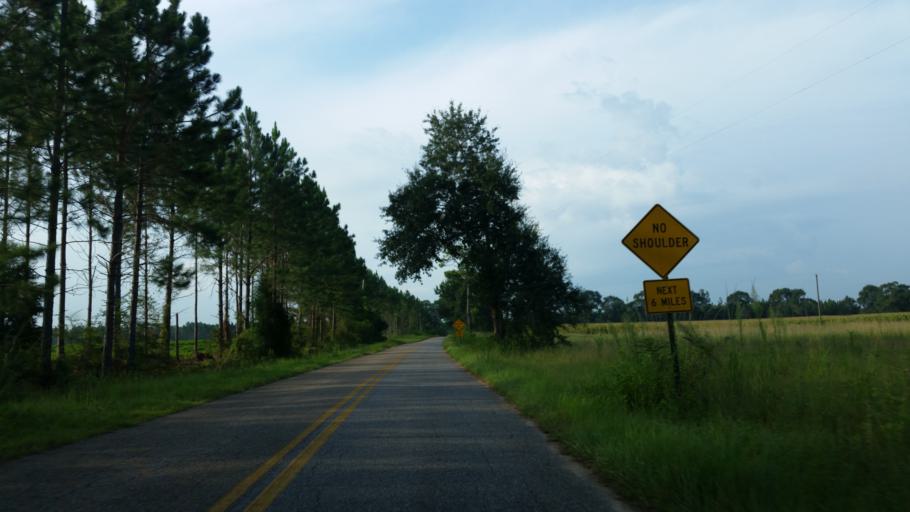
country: US
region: Alabama
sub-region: Escambia County
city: Atmore
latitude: 30.9827
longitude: -87.5713
